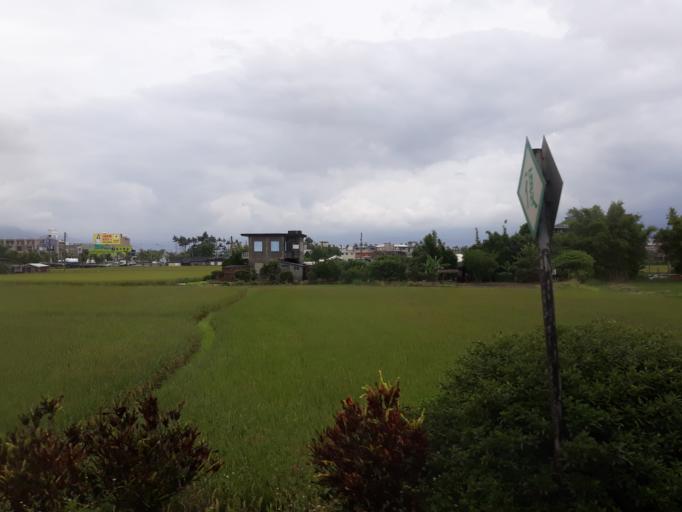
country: TW
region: Taiwan
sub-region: Yilan
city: Yilan
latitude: 24.6882
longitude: 121.7749
